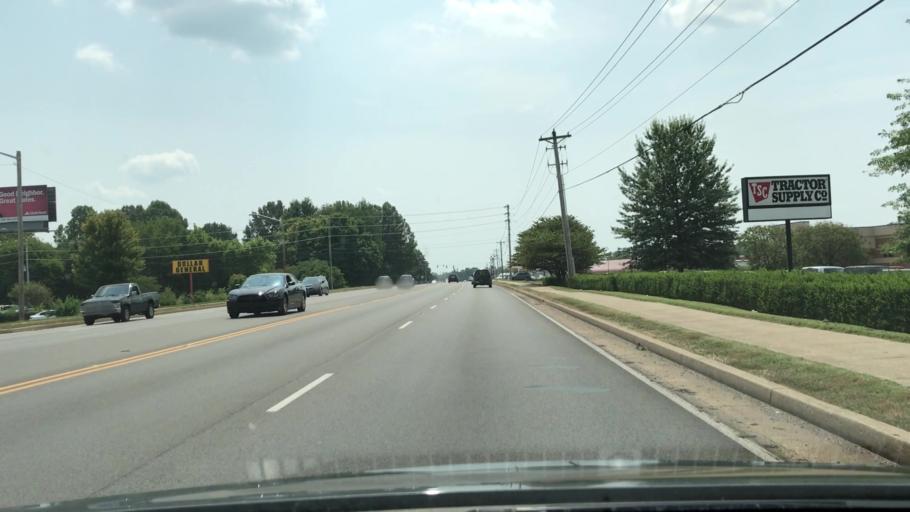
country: US
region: Kentucky
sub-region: Warren County
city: Plano
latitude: 36.9232
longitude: -86.4102
